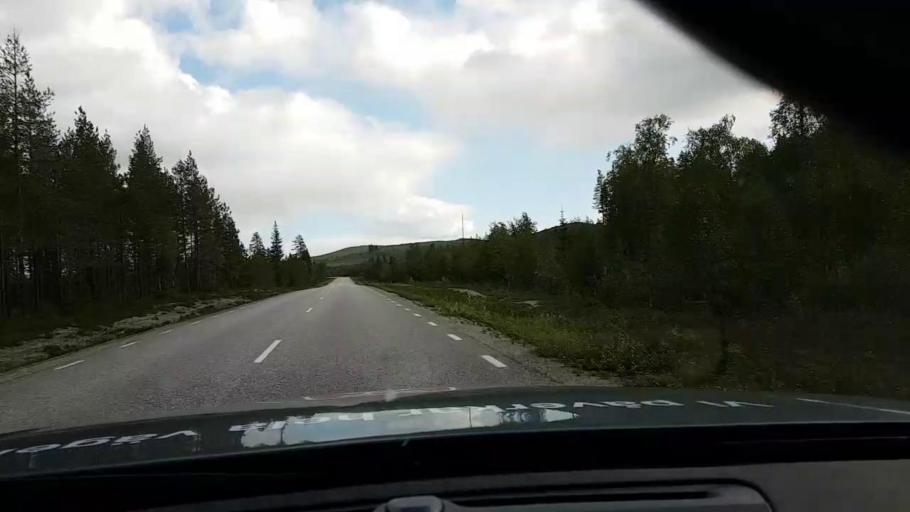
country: SE
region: Vaesternorrland
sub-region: OErnskoeldsviks Kommun
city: Bredbyn
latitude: 63.6833
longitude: 17.7796
